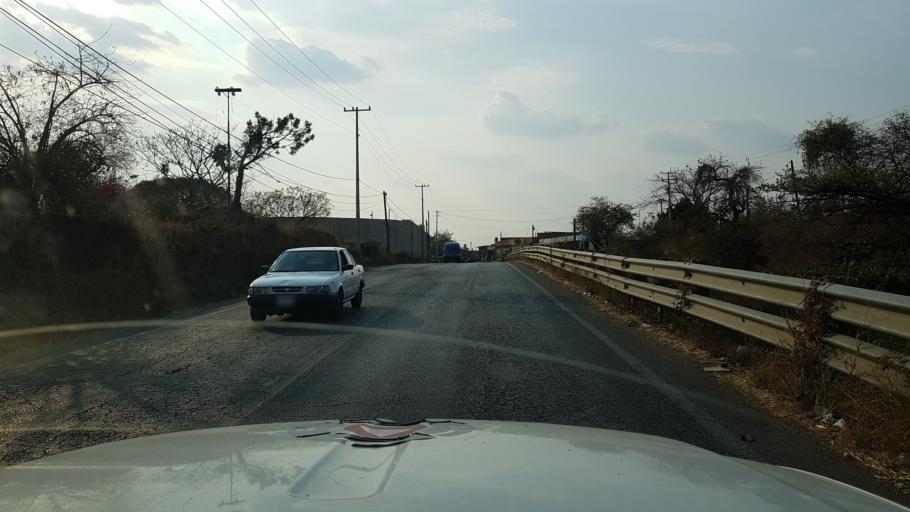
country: MX
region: Morelos
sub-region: Yecapixtla
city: Yecapixtla
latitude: 18.8883
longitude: -98.8753
